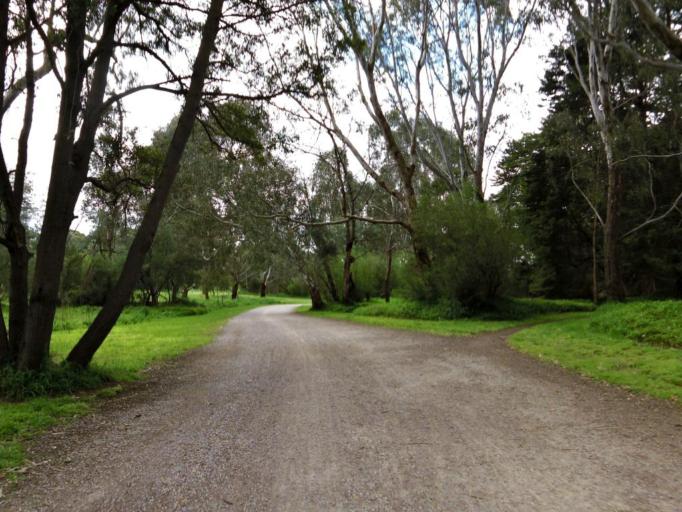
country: AU
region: Victoria
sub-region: Manningham
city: Bulleen
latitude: -37.7670
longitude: 145.0712
